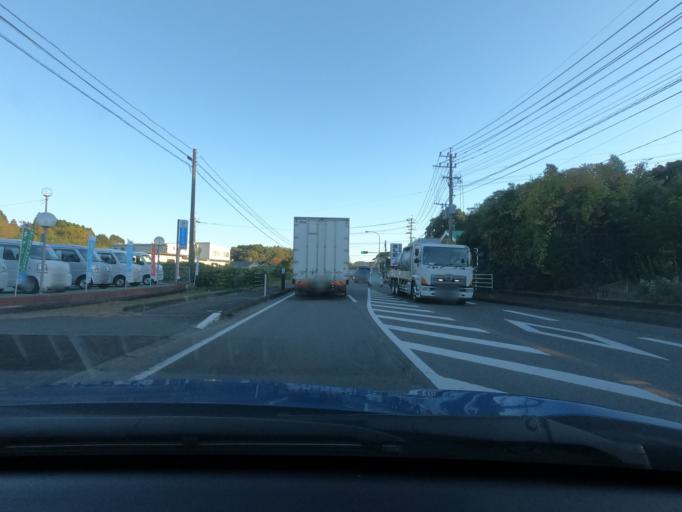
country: JP
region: Kagoshima
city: Satsumasendai
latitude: 31.8426
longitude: 130.2806
